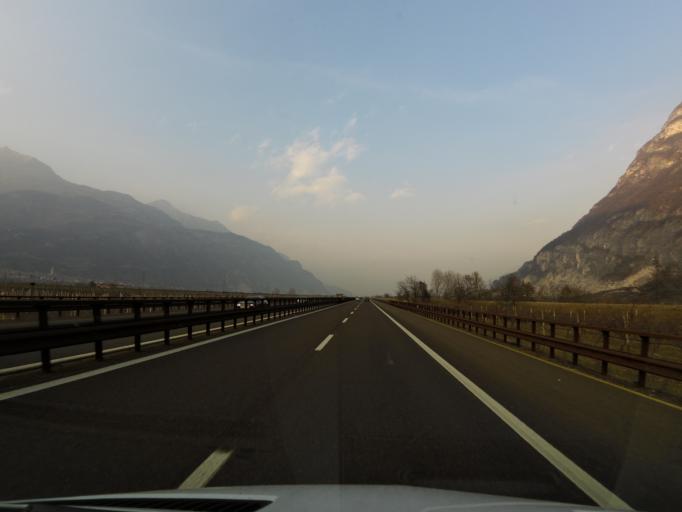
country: IT
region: Trentino-Alto Adige
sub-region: Provincia di Trento
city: Aldeno
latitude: 45.9645
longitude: 11.1066
